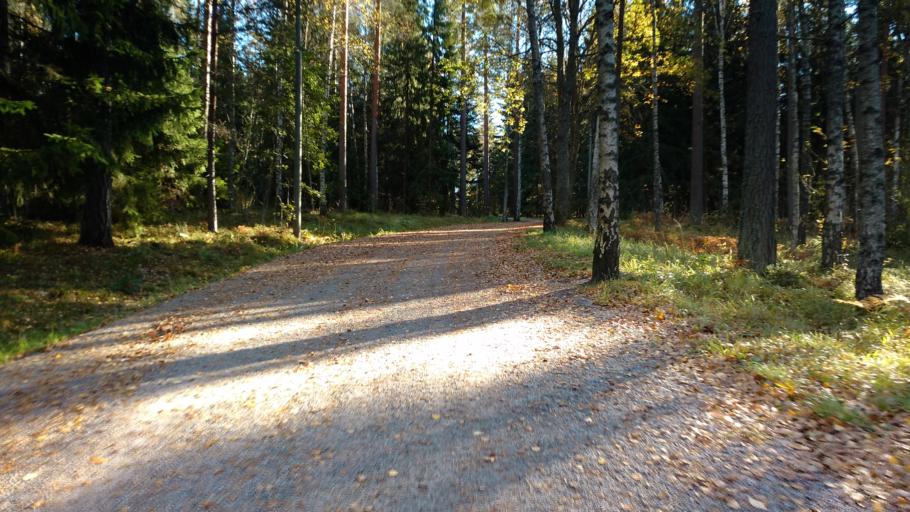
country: FI
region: Varsinais-Suomi
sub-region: Salo
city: Salo
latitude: 60.3963
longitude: 23.1747
